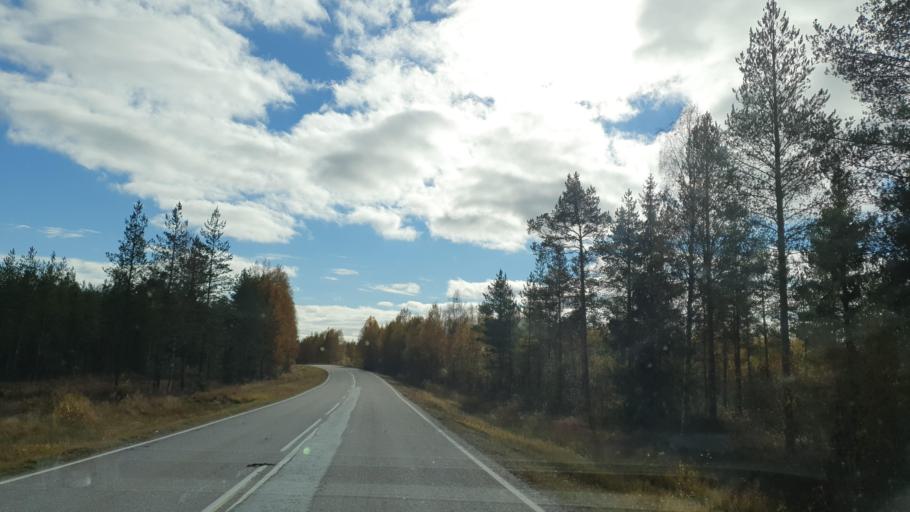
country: FI
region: Kainuu
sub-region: Kehys-Kainuu
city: Puolanka
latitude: 64.9313
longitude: 27.6042
